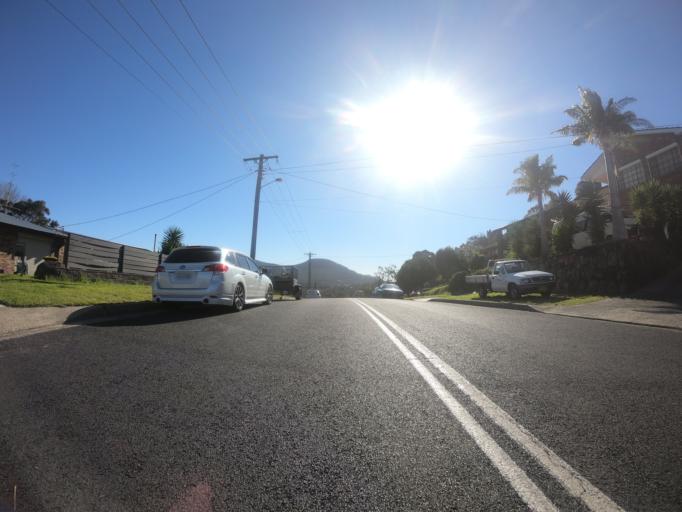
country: AU
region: New South Wales
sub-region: Wollongong
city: Cordeaux Heights
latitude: -34.4432
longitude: 150.8505
